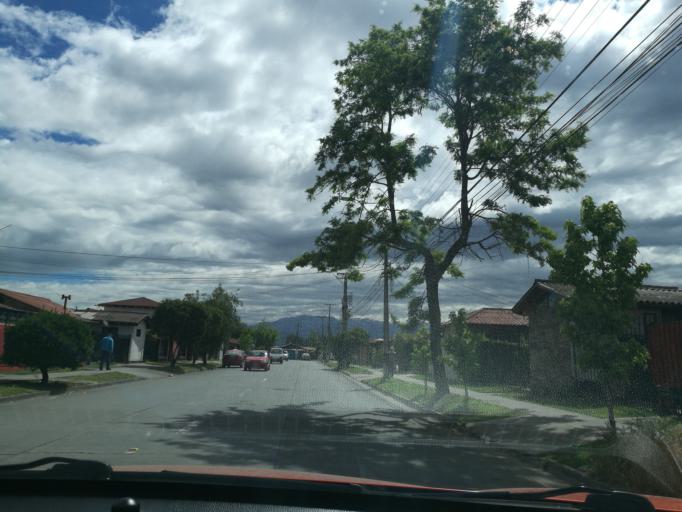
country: CL
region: O'Higgins
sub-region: Provincia de Cachapoal
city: Rancagua
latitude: -34.1341
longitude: -70.7370
